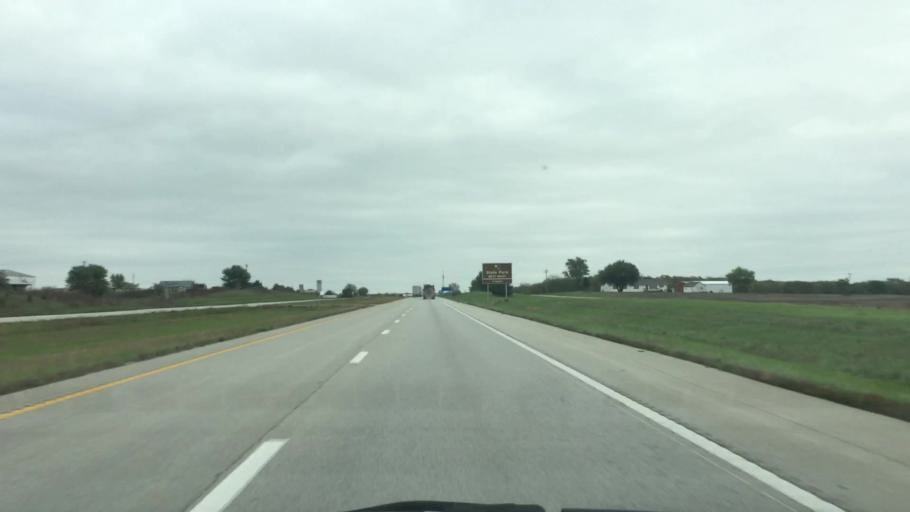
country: US
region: Missouri
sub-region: Clinton County
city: Cameron
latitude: 39.8431
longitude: -94.1812
